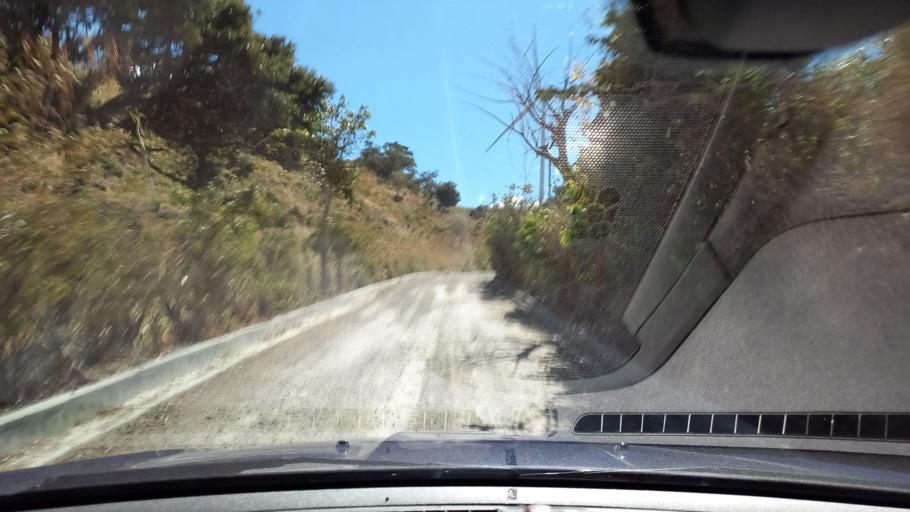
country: SV
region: Santa Ana
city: Metapan
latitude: 14.3731
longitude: -89.4884
